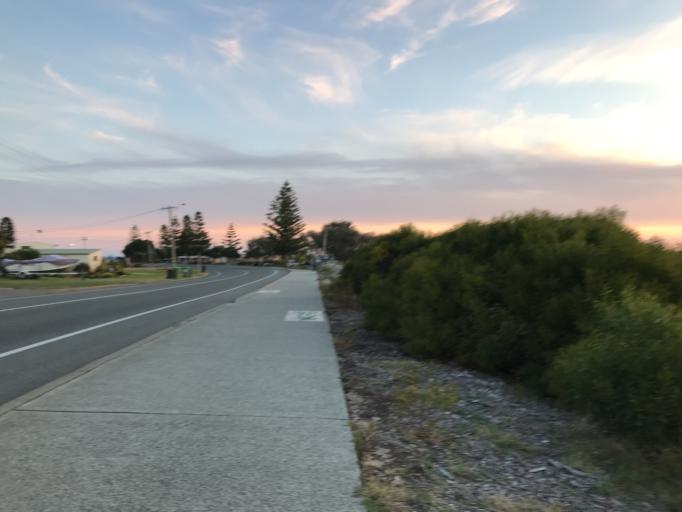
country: AU
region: Western Australia
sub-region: Rockingham
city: Shoalwater
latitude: -32.3028
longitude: 115.7027
